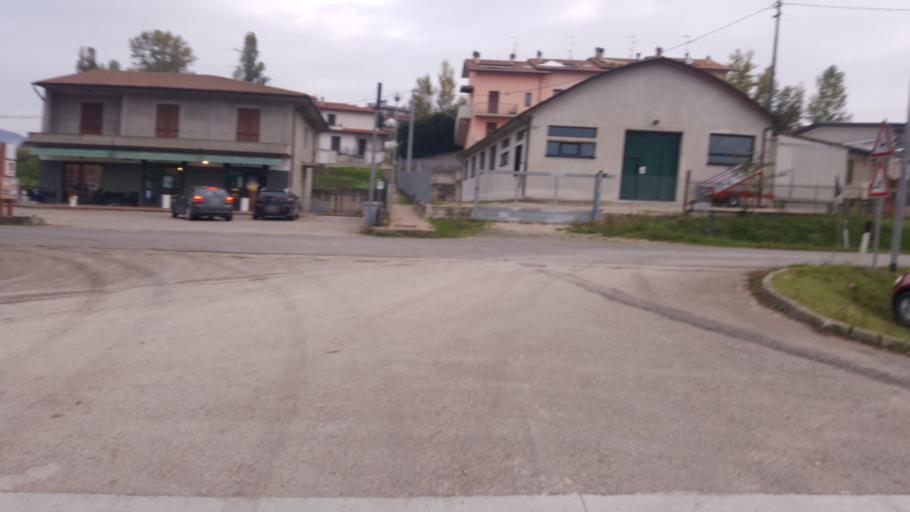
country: IT
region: Umbria
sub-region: Provincia di Perugia
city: Trestina
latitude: 43.3741
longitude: 12.2021
